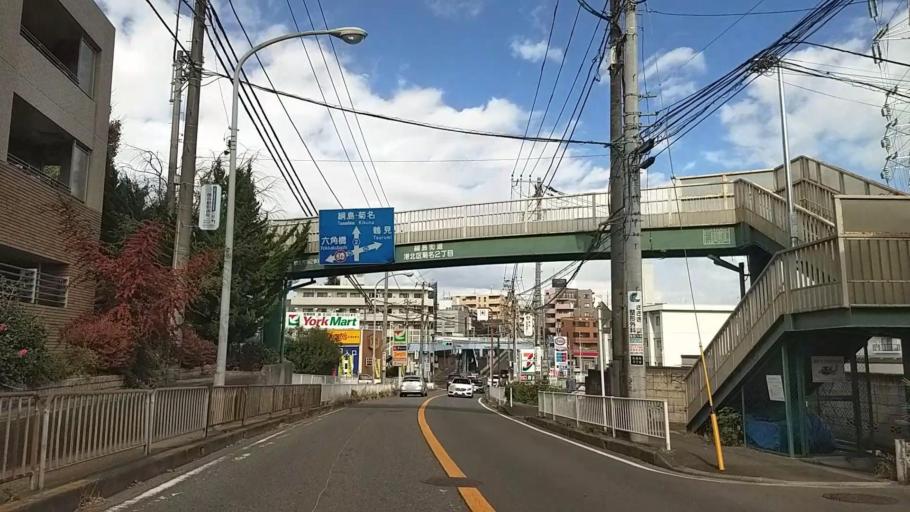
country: JP
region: Kanagawa
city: Yokohama
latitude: 35.5002
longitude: 139.6367
